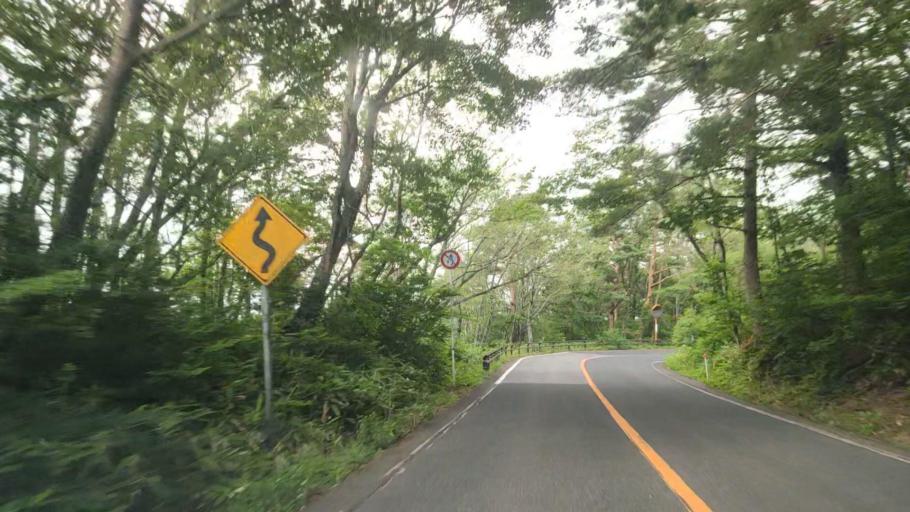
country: JP
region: Tottori
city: Yonago
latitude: 35.3666
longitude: 133.5180
